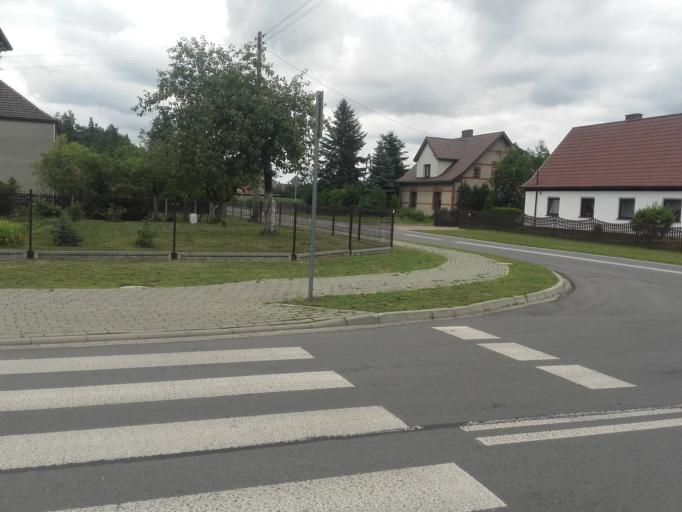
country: PL
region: Opole Voivodeship
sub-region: Powiat oleski
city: Olesno
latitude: 50.9194
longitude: 18.4831
